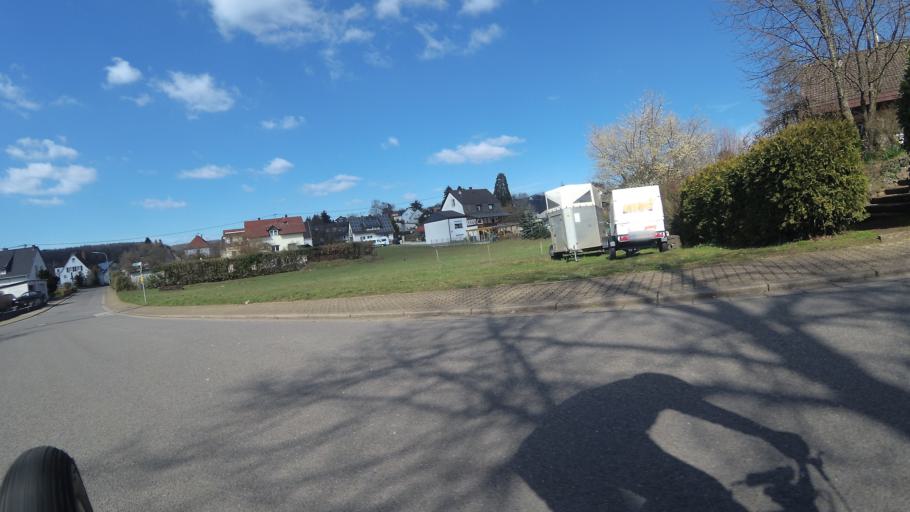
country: DE
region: Saarland
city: Beckingen
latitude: 49.3845
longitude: 6.7072
